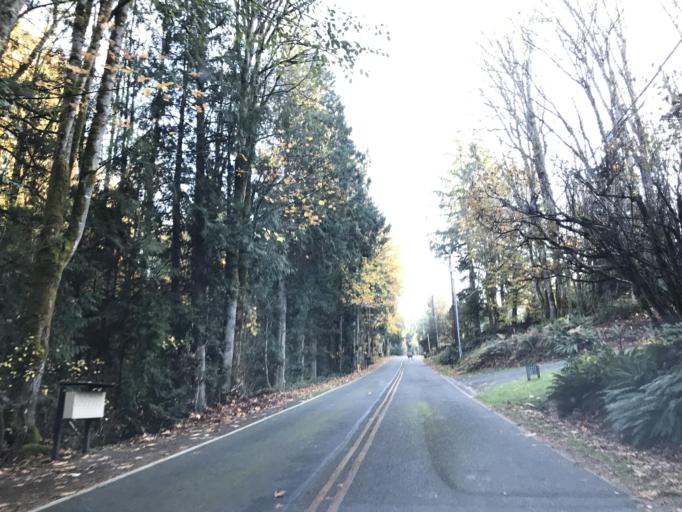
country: US
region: Washington
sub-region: Whatcom County
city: Geneva
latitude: 48.7468
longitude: -122.4099
